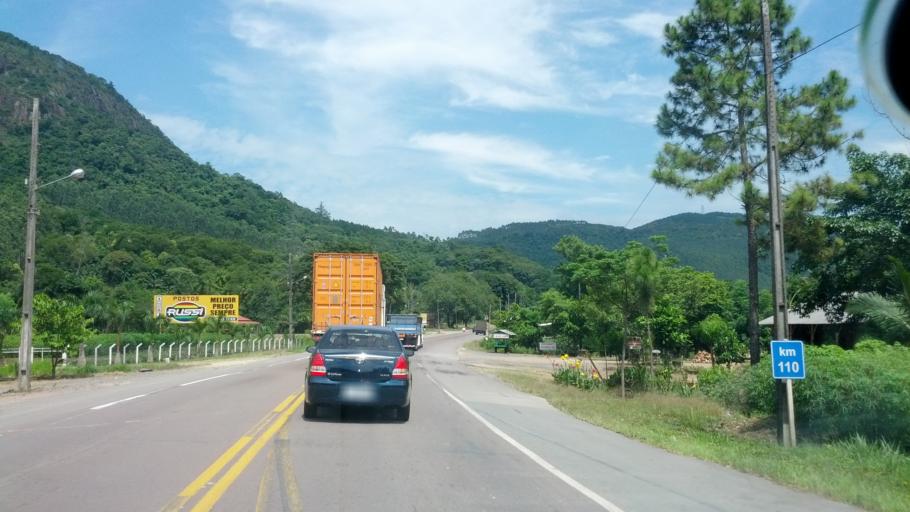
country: BR
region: Santa Catarina
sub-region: Ibirama
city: Ibirama
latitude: -27.0828
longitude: -49.4440
